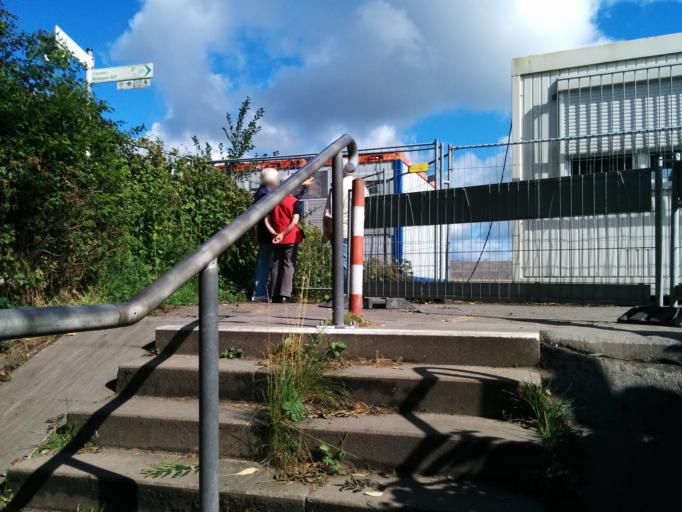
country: DE
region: Schleswig-Holstein
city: Wedel
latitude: 53.5662
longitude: 9.7324
